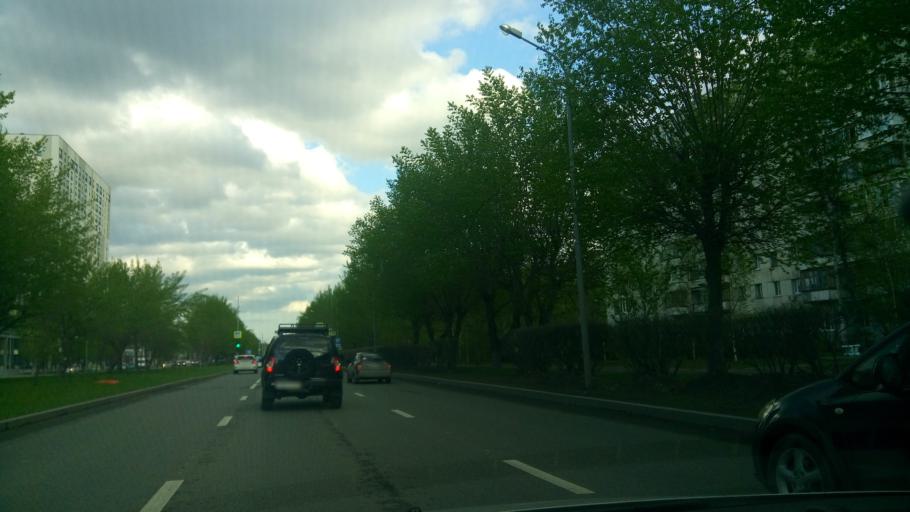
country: RU
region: Tjumen
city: Tyumen
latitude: 57.1406
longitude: 65.5908
